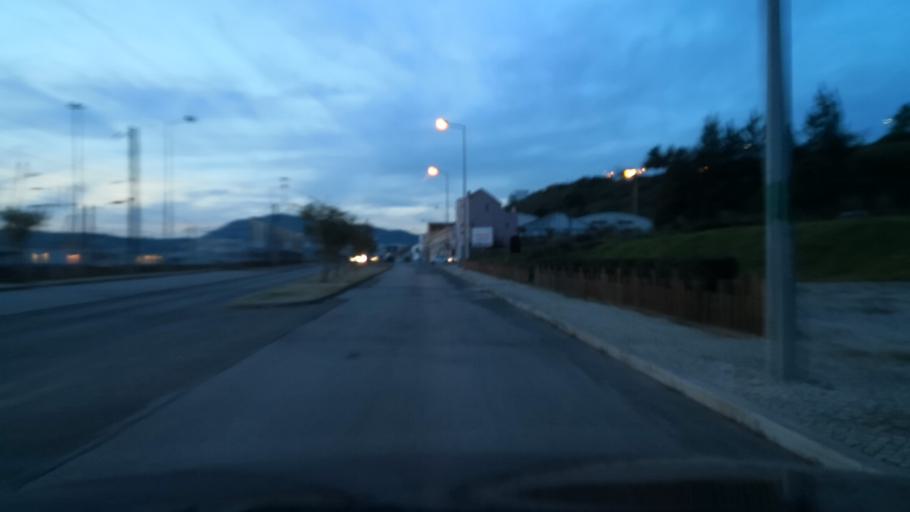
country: PT
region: Setubal
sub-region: Setubal
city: Setubal
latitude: 38.5193
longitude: -8.8763
